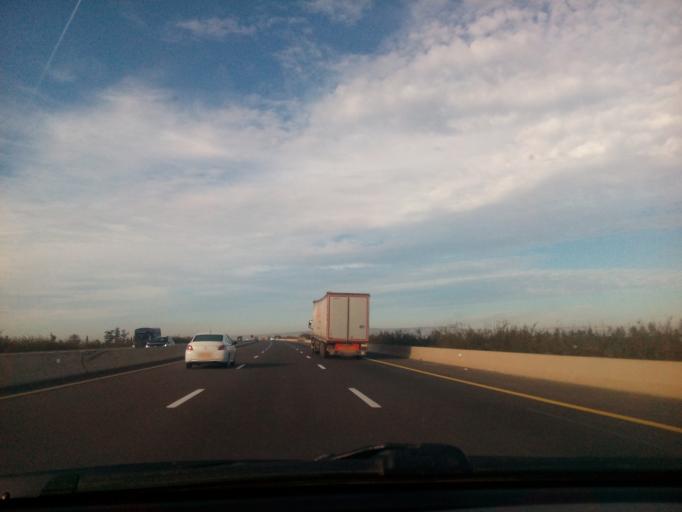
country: DZ
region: Mascara
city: Sig
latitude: 35.5840
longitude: -0.1972
